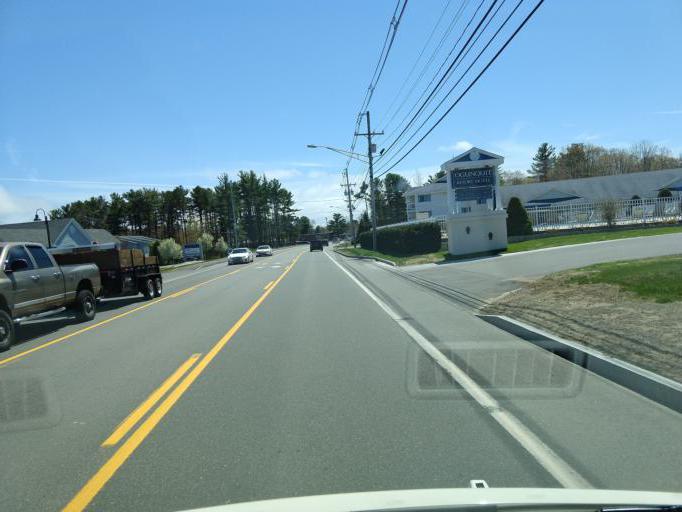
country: US
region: Maine
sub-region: York County
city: Ogunquit
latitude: 43.2684
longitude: -70.5975
